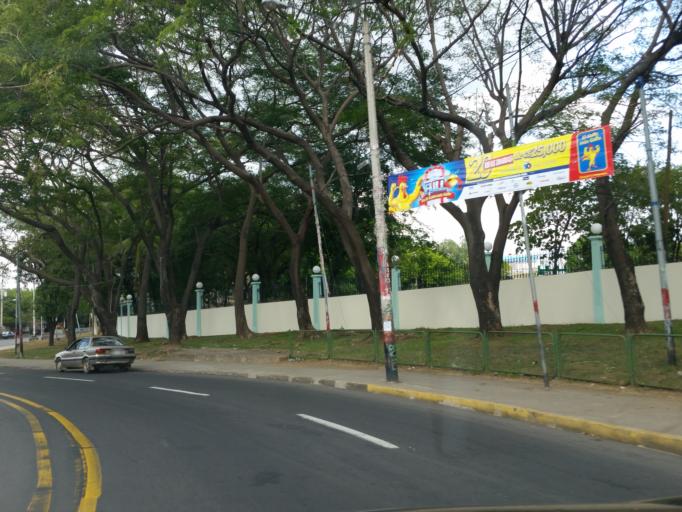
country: NI
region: Managua
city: Managua
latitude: 12.1453
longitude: -86.2729
